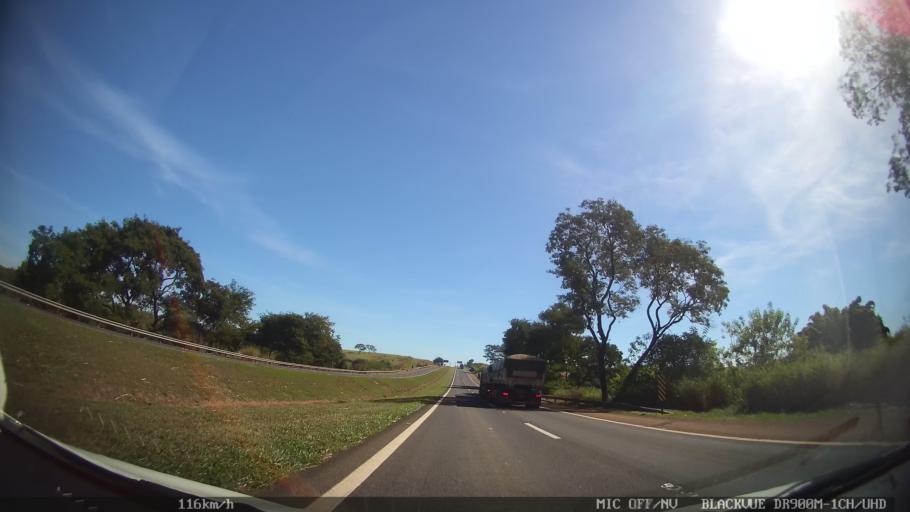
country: BR
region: Sao Paulo
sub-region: Santa Rita Do Passa Quatro
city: Santa Rita do Passa Quatro
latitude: -21.7633
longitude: -47.5544
